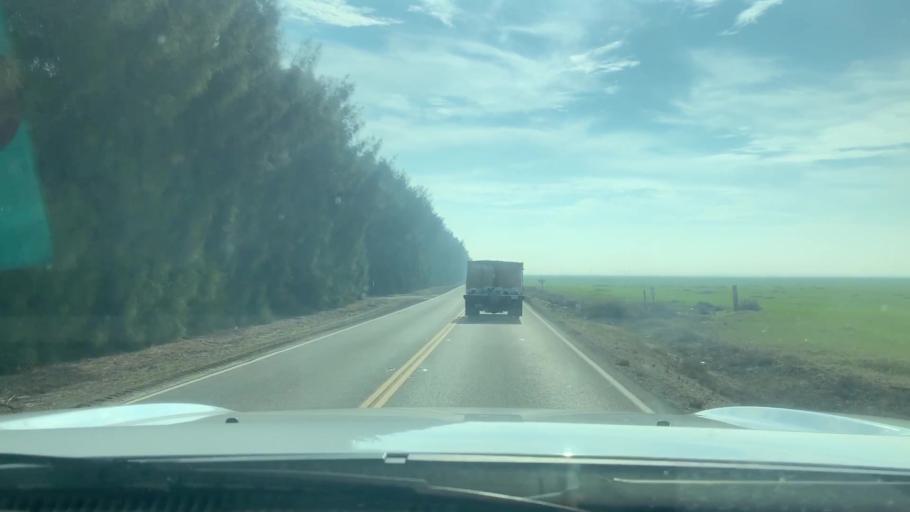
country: US
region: California
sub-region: Kern County
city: Lost Hills
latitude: 35.5138
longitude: -119.7505
